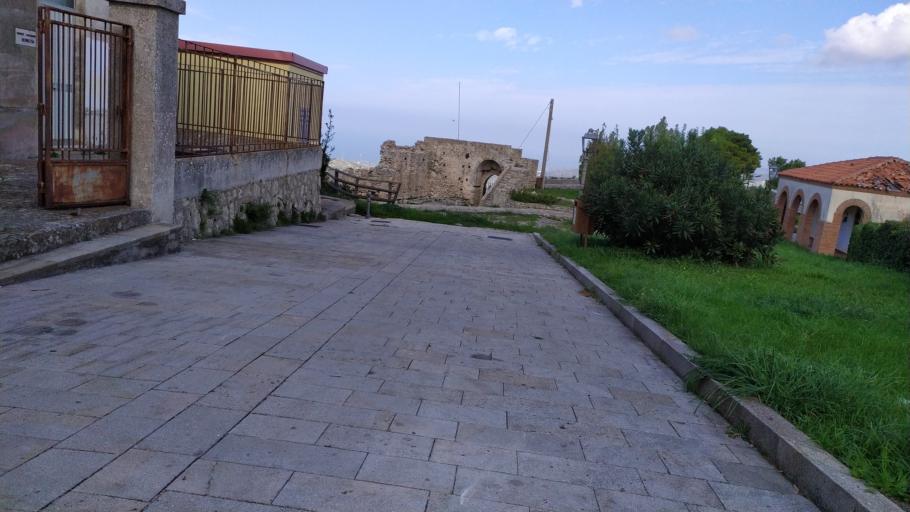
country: IT
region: Sicily
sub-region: Messina
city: Rometta
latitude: 38.1736
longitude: 15.4165
